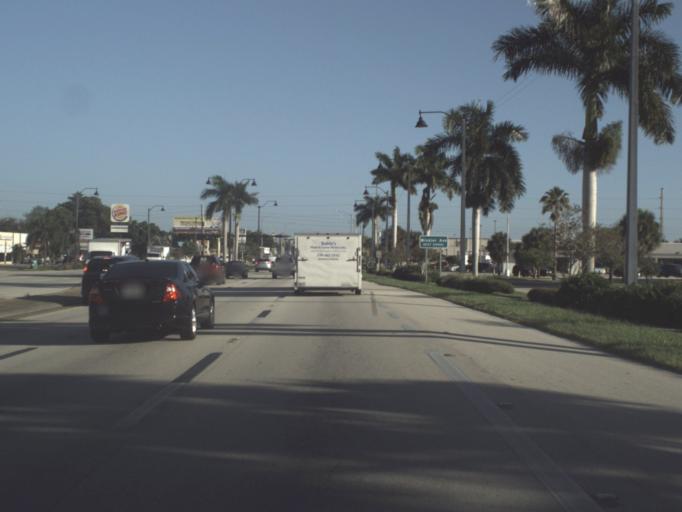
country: US
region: Florida
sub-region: Lee County
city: Pine Manor
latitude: 26.6023
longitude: -81.8716
